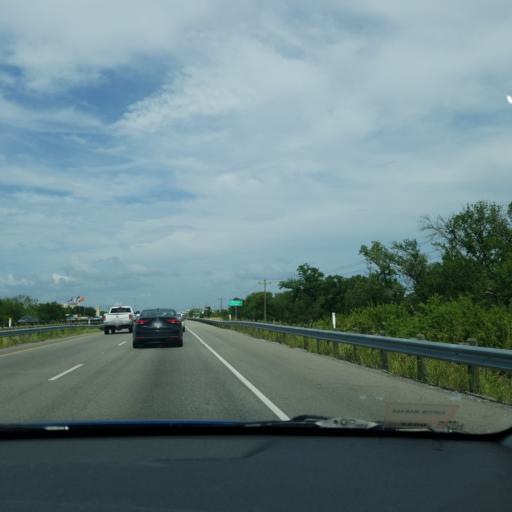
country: US
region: Texas
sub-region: Travis County
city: Manor
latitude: 30.3488
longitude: -97.5505
